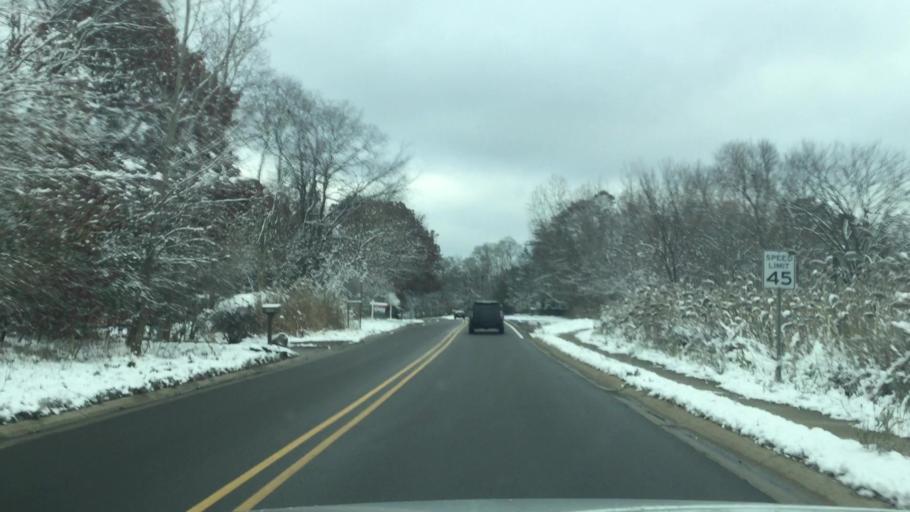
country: US
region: Michigan
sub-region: Oakland County
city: West Bloomfield Township
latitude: 42.5697
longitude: -83.4097
